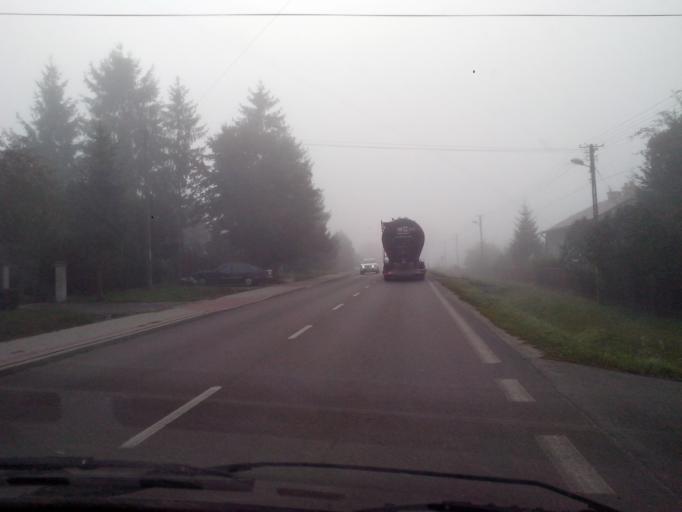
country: PL
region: Subcarpathian Voivodeship
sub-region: Przemysl
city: Przemysl
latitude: 49.7955
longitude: 22.7186
